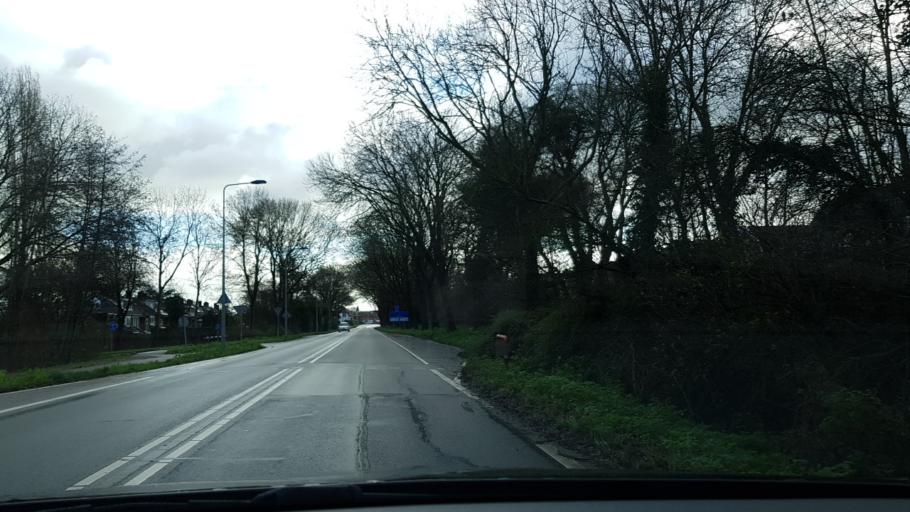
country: NL
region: North Holland
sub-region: Gemeente Uithoorn
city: Uithoorn
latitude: 52.2364
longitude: 4.8243
